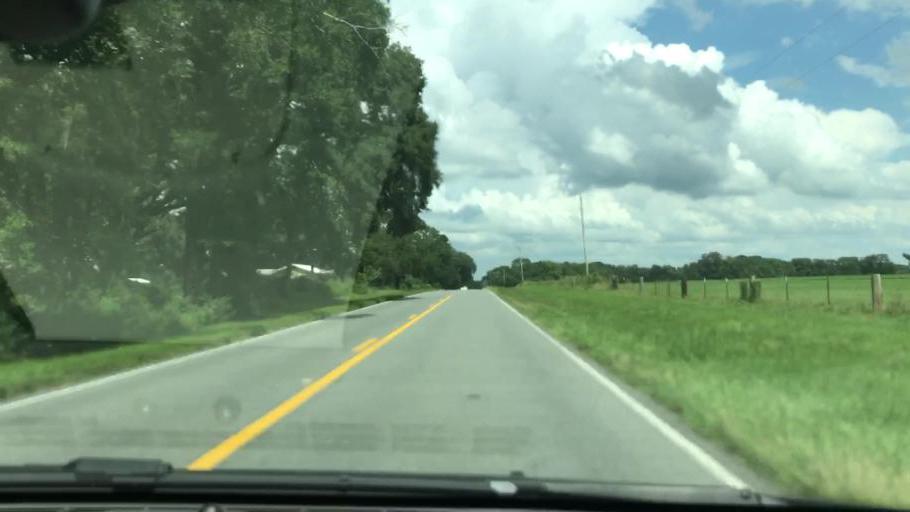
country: US
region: Florida
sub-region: Jackson County
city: Malone
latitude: 30.8950
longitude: -85.1424
